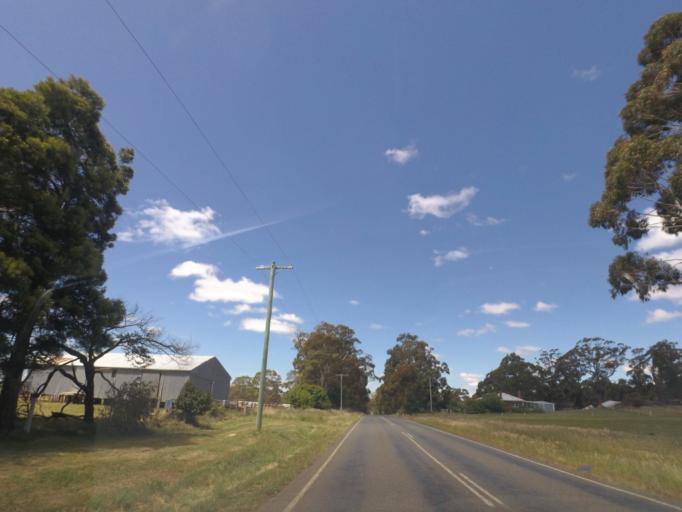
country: AU
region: Victoria
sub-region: Mount Alexander
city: Castlemaine
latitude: -37.3192
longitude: 144.2091
